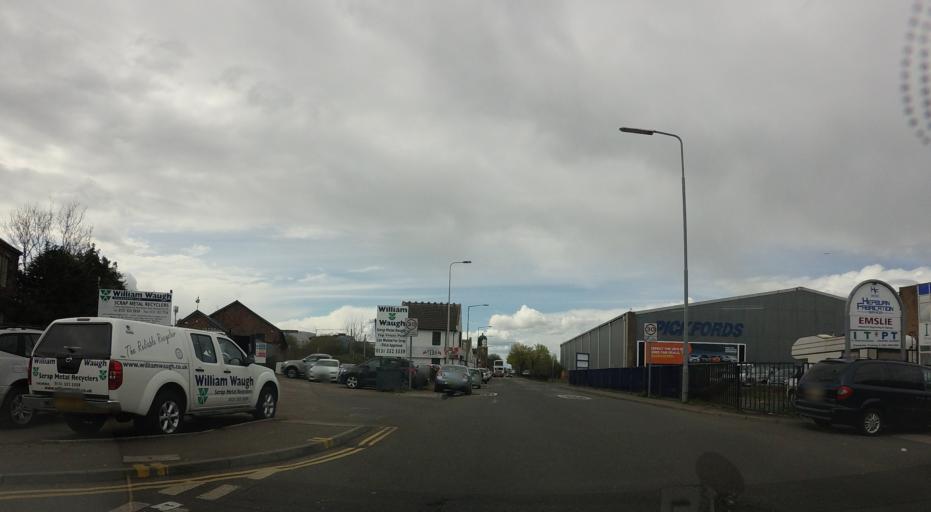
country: GB
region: Scotland
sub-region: Edinburgh
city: Edinburgh
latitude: 55.9814
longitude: -3.2258
